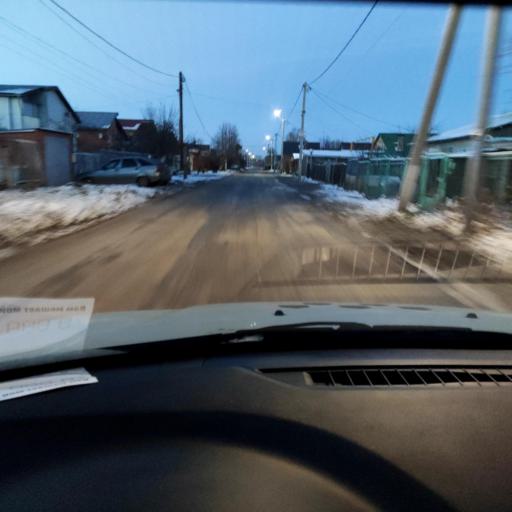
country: RU
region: Samara
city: Tol'yatti
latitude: 53.5649
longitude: 49.3898
